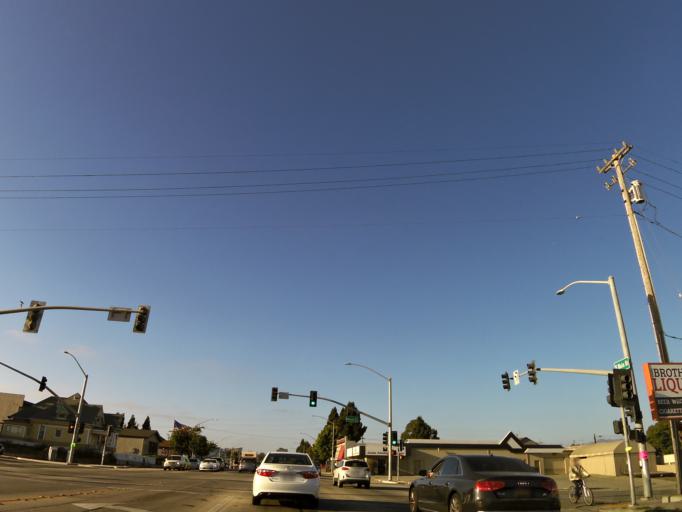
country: US
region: California
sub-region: Monterey County
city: Salinas
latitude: 36.6807
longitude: -121.6542
